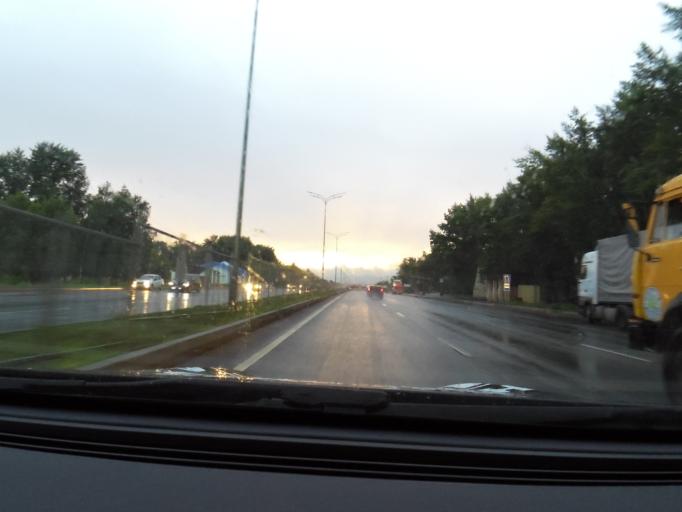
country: RU
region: Tatarstan
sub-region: Tukayevskiy Rayon
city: Naberezhnyye Chelny
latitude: 55.6734
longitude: 52.2912
